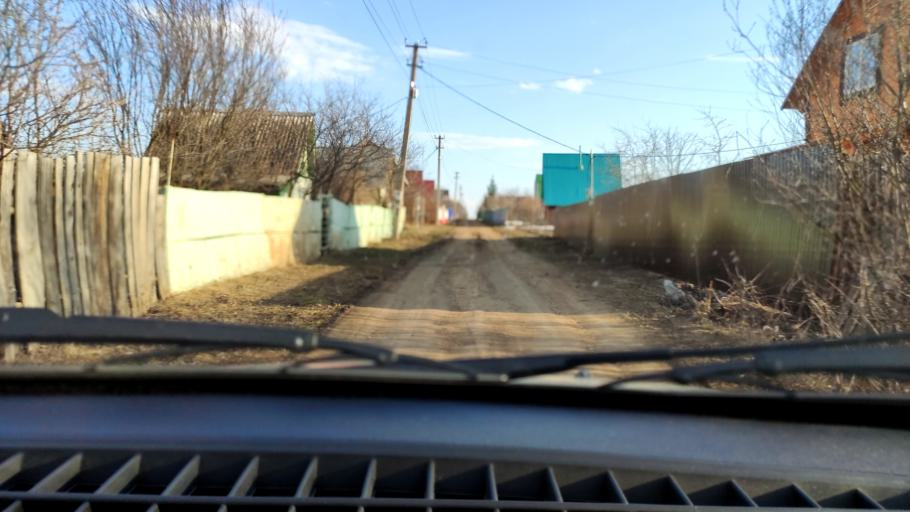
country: RU
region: Bashkortostan
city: Iglino
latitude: 54.8455
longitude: 56.4706
